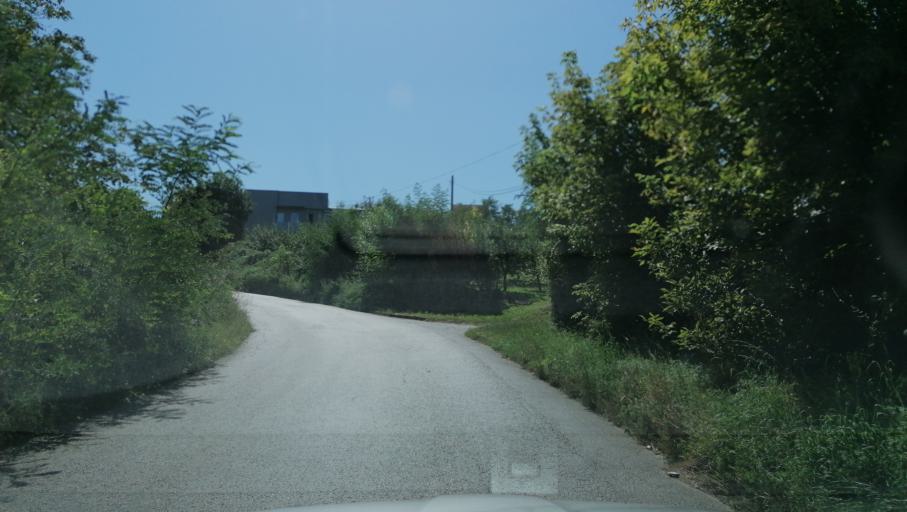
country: RS
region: Central Serbia
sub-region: Kolubarski Okrug
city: Valjevo
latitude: 44.2538
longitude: 19.8755
